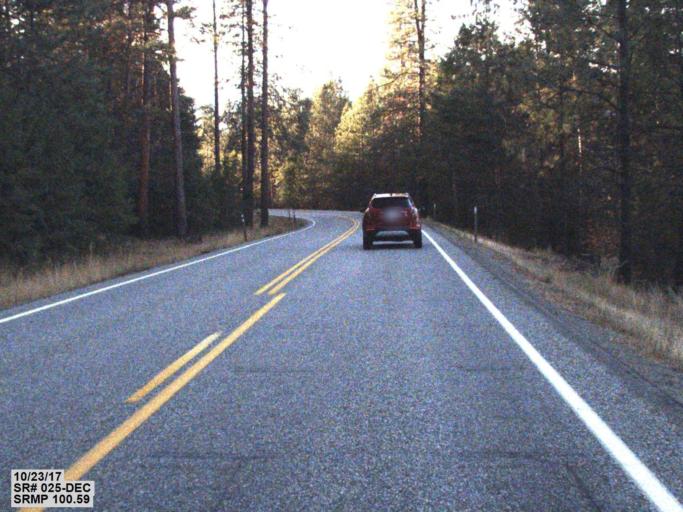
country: US
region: Washington
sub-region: Stevens County
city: Kettle Falls
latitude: 48.8152
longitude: -117.9718
